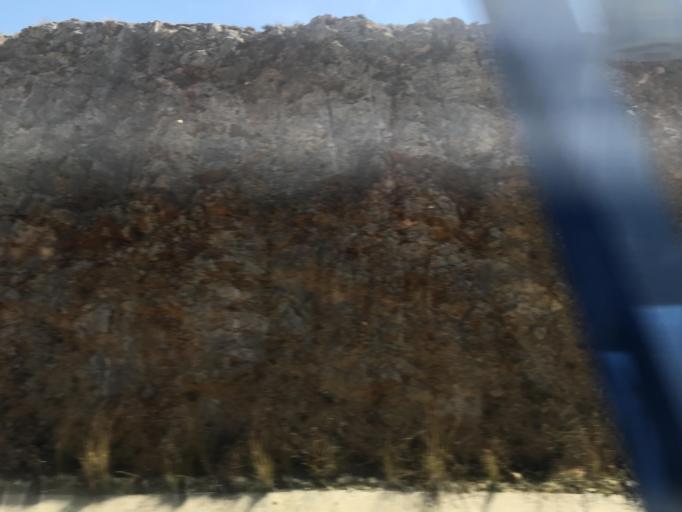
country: ES
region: Castille-La Mancha
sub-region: Provincia de Guadalajara
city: Anguita
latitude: 41.1235
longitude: -2.3454
